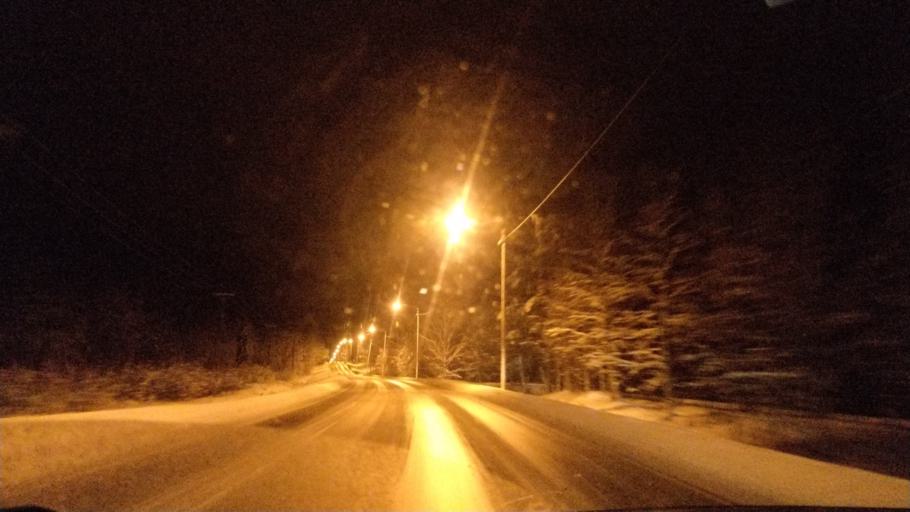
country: FI
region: Lapland
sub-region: Rovaniemi
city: Rovaniemi
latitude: 66.3019
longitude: 25.3543
